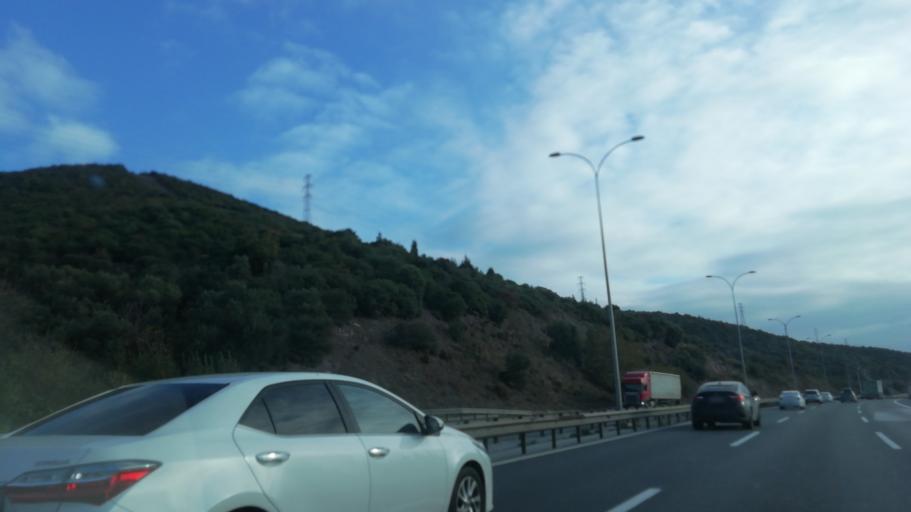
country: TR
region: Kocaeli
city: Hereke
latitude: 40.7798
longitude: 29.6641
